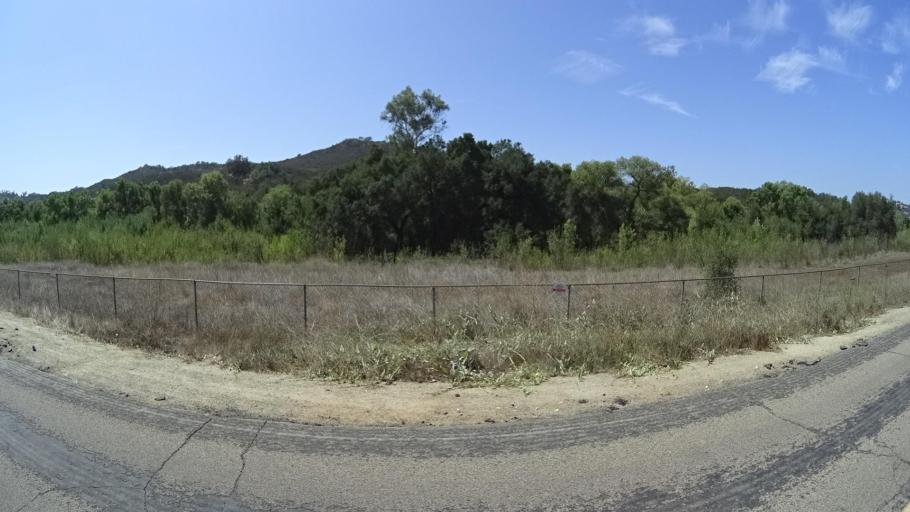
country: US
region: California
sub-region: San Diego County
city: Valley Center
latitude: 33.2236
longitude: -117.0474
